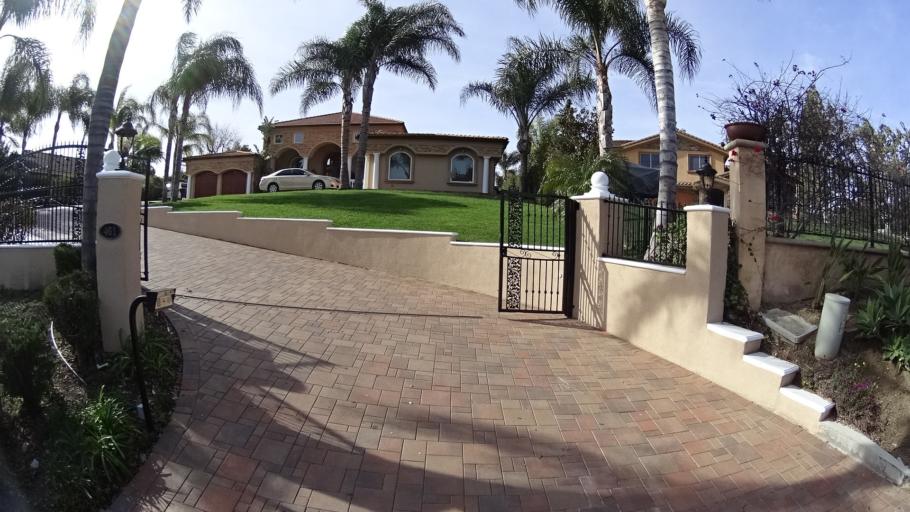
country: US
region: California
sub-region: Orange County
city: Yorba Linda
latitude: 33.8544
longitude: -117.7566
